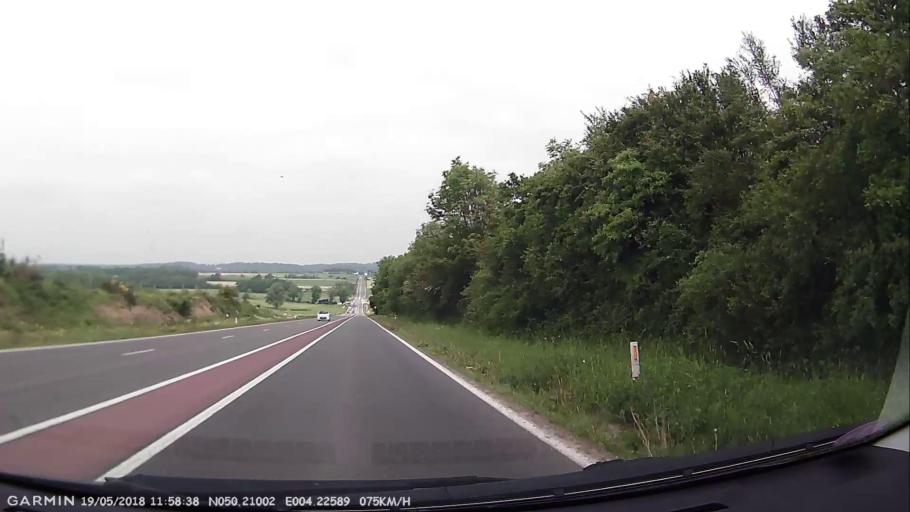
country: BE
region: Wallonia
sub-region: Province du Hainaut
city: Beaumont
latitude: 50.2102
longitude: 4.2259
